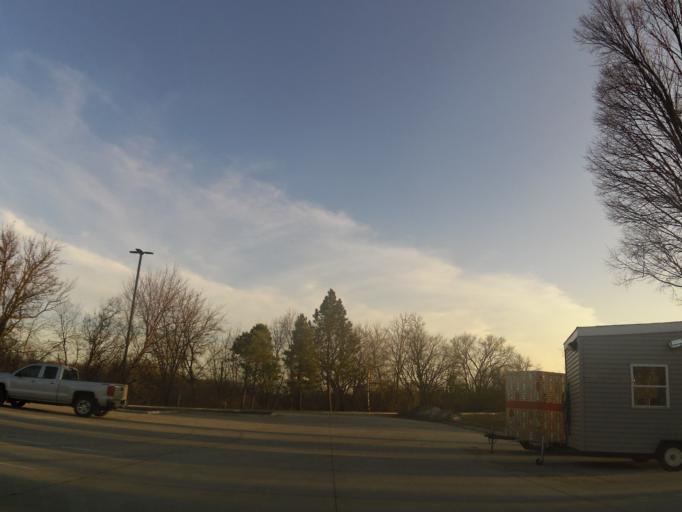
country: US
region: North Dakota
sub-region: Grand Forks County
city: Grand Forks
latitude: 47.8995
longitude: -97.0253
